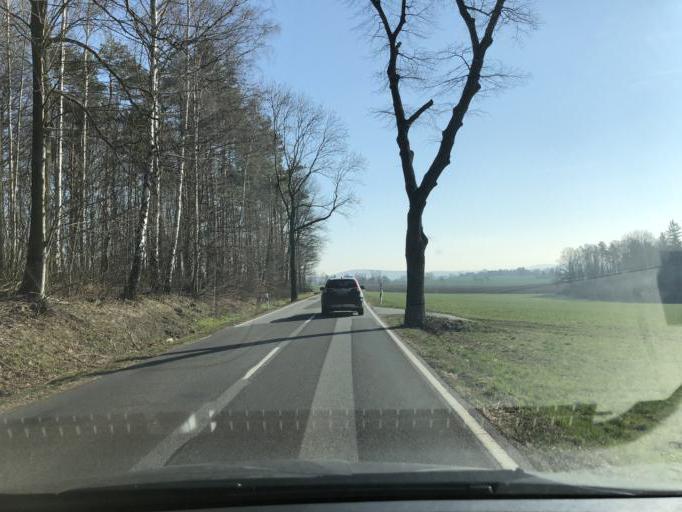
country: DE
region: Saxony
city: Frankenthal
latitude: 51.1501
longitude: 14.1073
